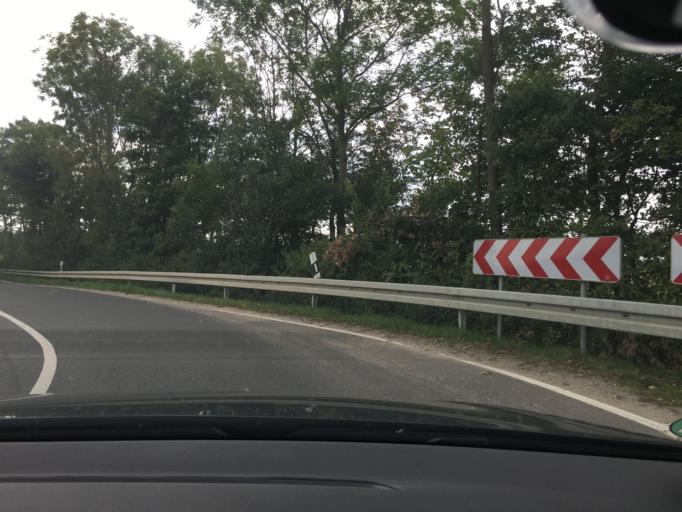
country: DE
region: North Rhine-Westphalia
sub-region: Regierungsbezirk Koln
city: Titz
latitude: 51.0453
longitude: 6.4625
